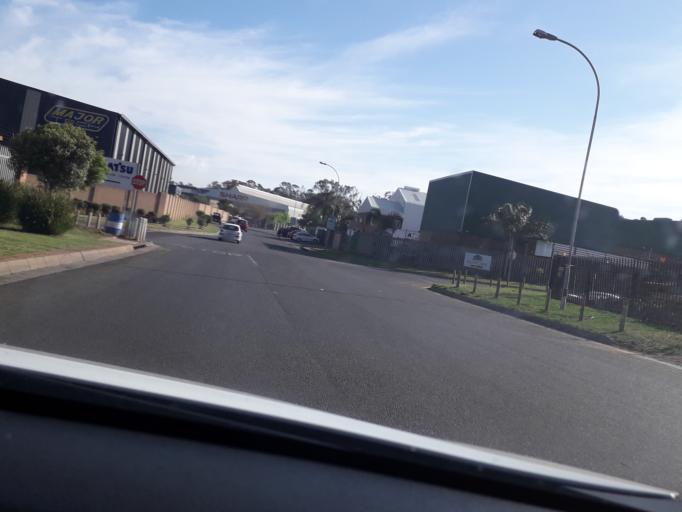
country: ZA
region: Gauteng
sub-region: City of Johannesburg Metropolitan Municipality
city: Modderfontein
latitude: -26.1597
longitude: 28.1830
